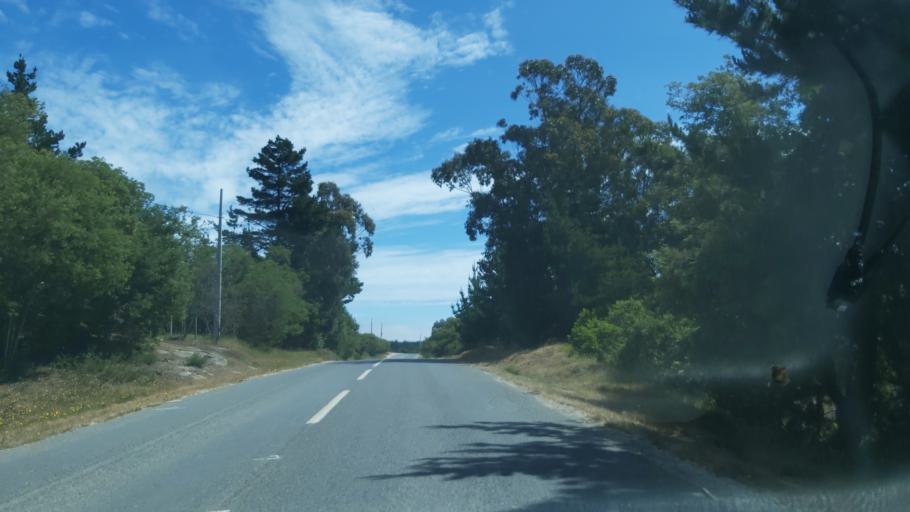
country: CL
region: Maule
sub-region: Provincia de Talca
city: Constitucion
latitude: -35.5635
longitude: -72.5925
